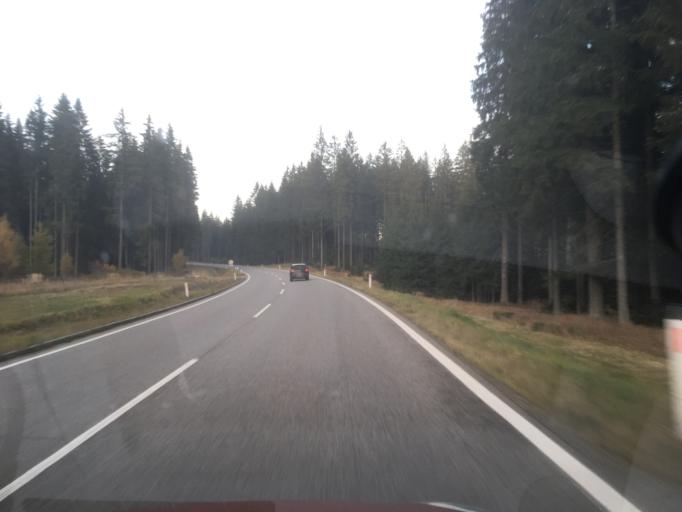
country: AT
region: Lower Austria
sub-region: Politischer Bezirk Zwettl
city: Langschlag
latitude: 48.5636
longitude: 14.7285
